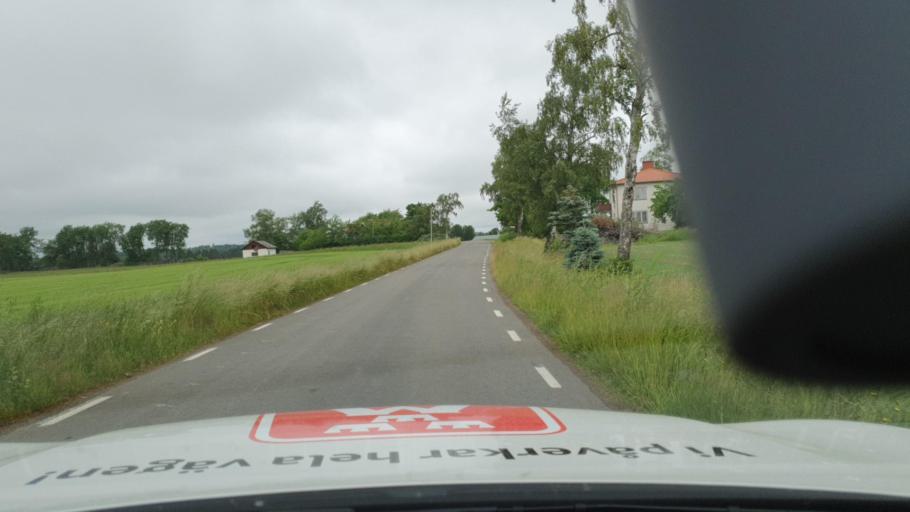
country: SE
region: Vaestra Goetaland
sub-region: Tidaholms Kommun
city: Olofstorp
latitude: 58.3848
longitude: 13.9982
